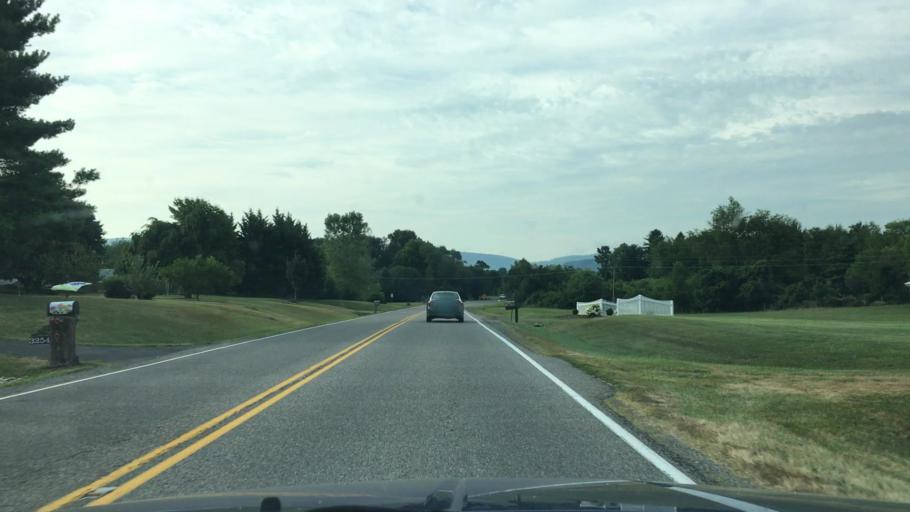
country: US
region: Virginia
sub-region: City of Waynesboro
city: Waynesboro
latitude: 38.1005
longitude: -78.9002
